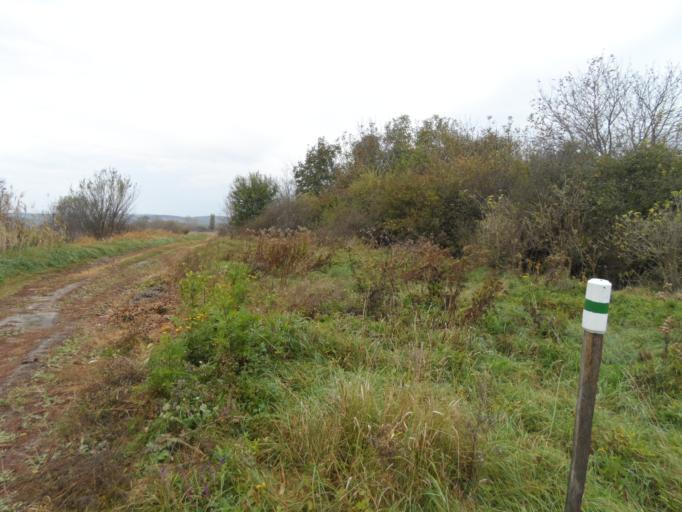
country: HU
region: Fejer
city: Kincsesbanya
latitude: 47.2478
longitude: 18.3233
